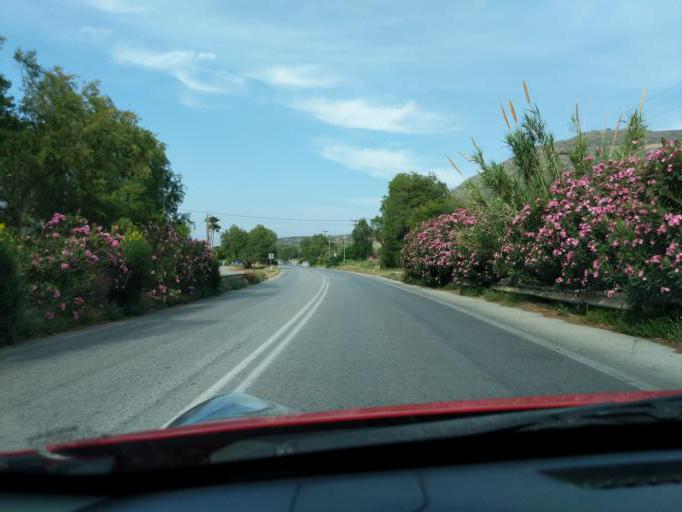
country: GR
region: Crete
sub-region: Nomos Rethymnis
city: Atsipopoulon
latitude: 35.3524
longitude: 24.3634
